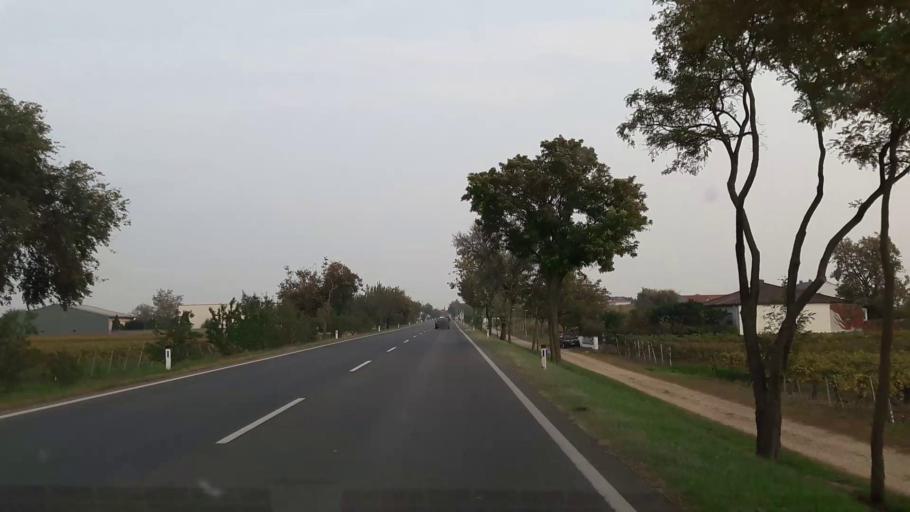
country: AT
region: Burgenland
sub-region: Politischer Bezirk Neusiedl am See
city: Gols
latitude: 47.9100
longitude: 16.8917
